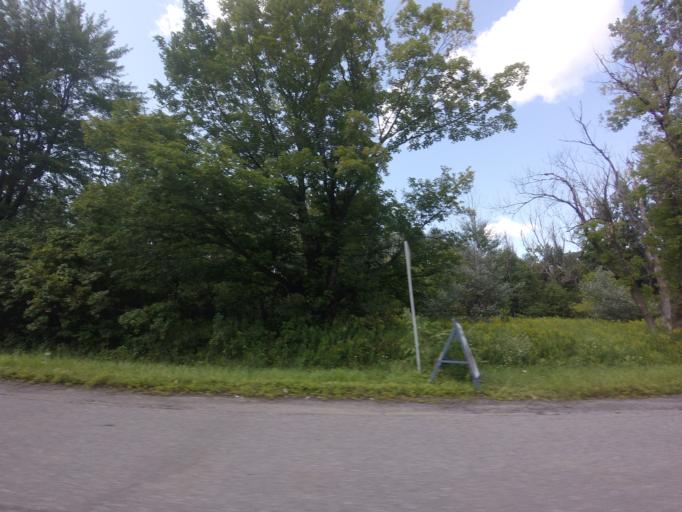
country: CA
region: Ontario
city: Bells Corners
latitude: 45.3430
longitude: -75.8855
